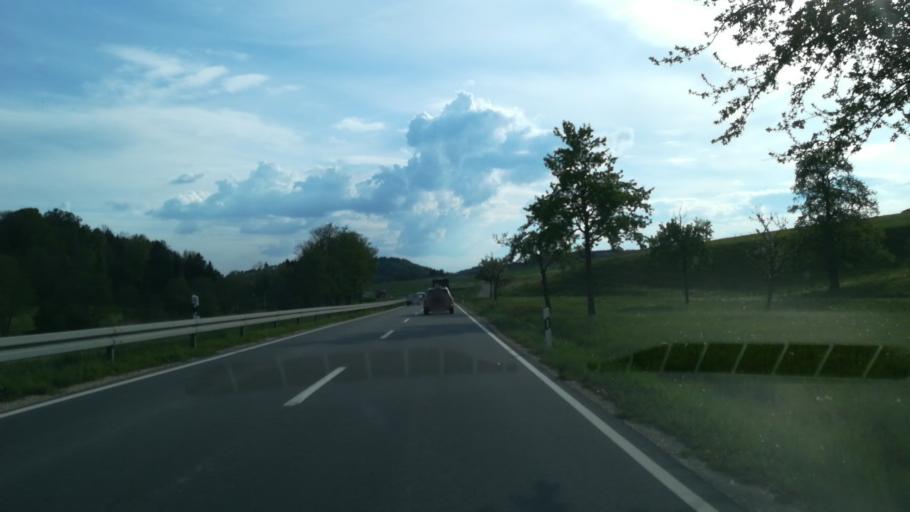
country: DE
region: Baden-Wuerttemberg
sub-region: Freiburg Region
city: Muhlingen
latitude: 47.9122
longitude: 9.0407
